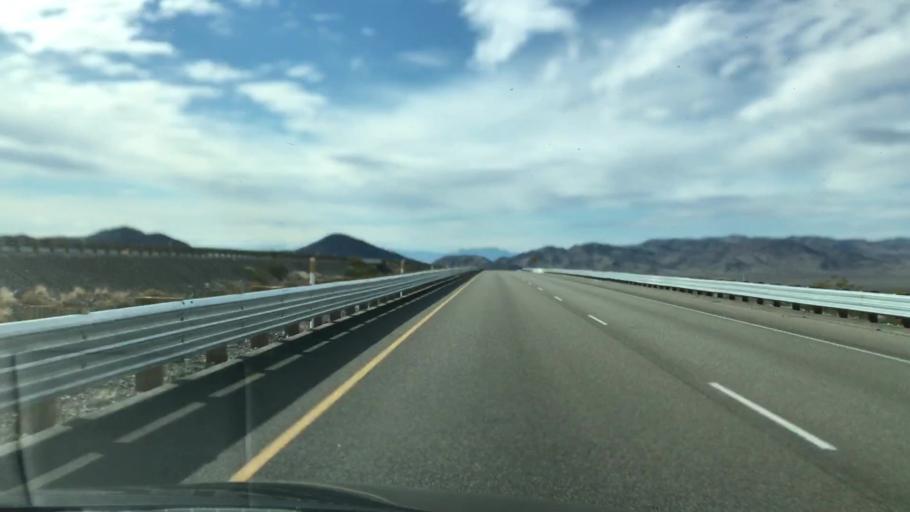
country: US
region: Nevada
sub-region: Nye County
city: Pahrump
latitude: 36.5986
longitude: -115.9960
